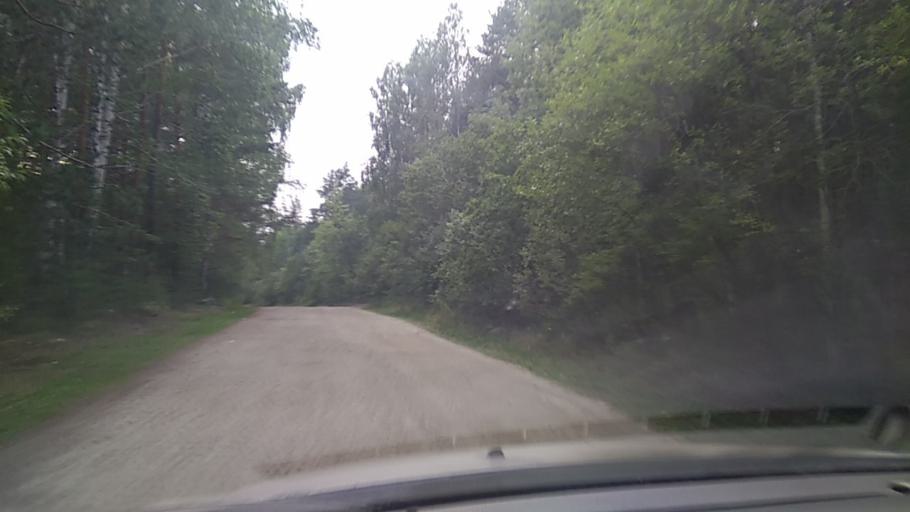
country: RU
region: Chelyabinsk
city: Kyshtym
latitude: 55.6775
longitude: 60.5877
